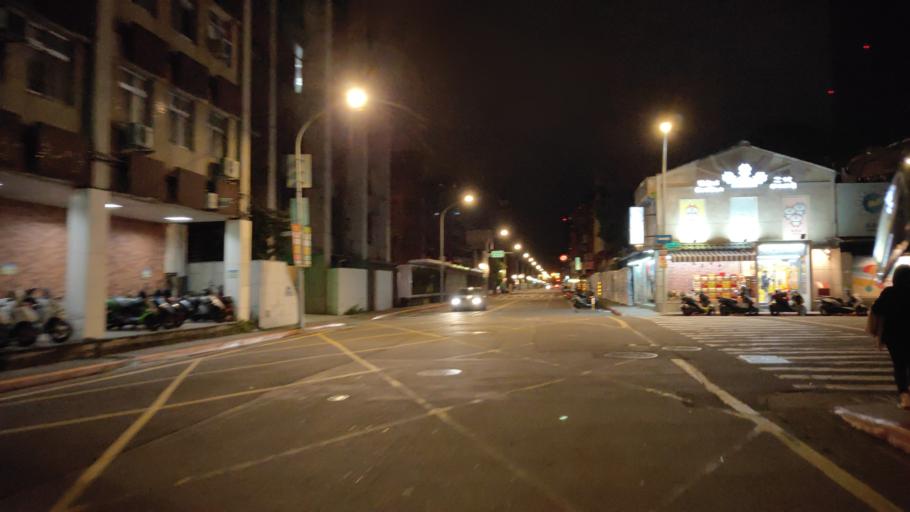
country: TW
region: Taipei
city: Taipei
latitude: 25.0152
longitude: 121.5321
